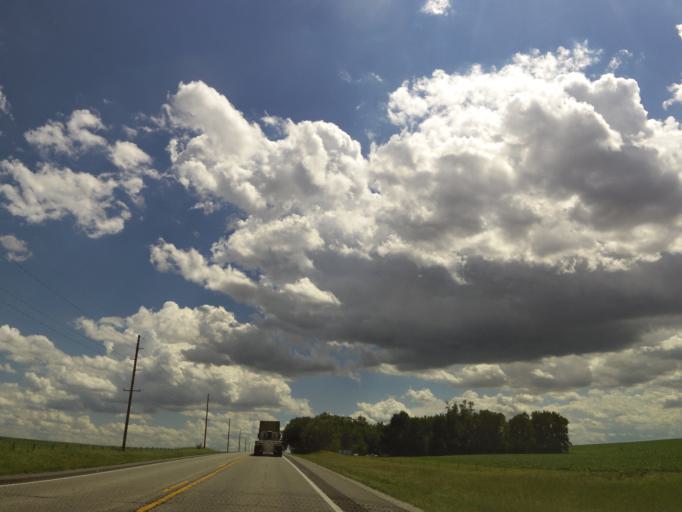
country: US
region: Iowa
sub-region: Benton County
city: Urbana
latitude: 42.2582
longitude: -91.8906
